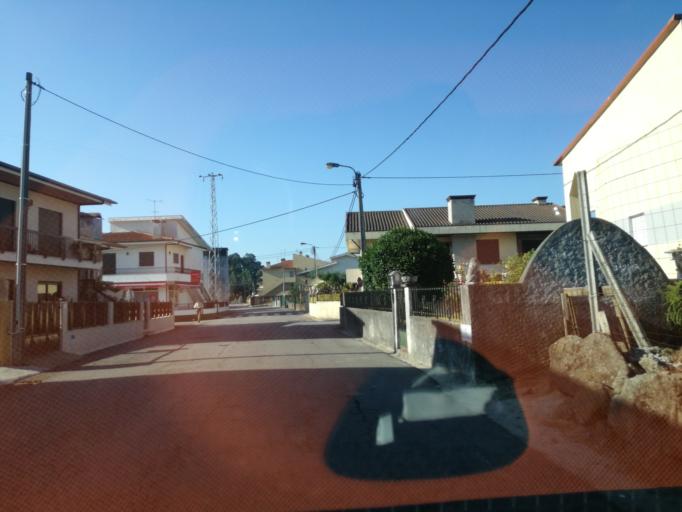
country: PT
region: Porto
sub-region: Maia
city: Nogueira
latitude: 41.2621
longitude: -8.5745
